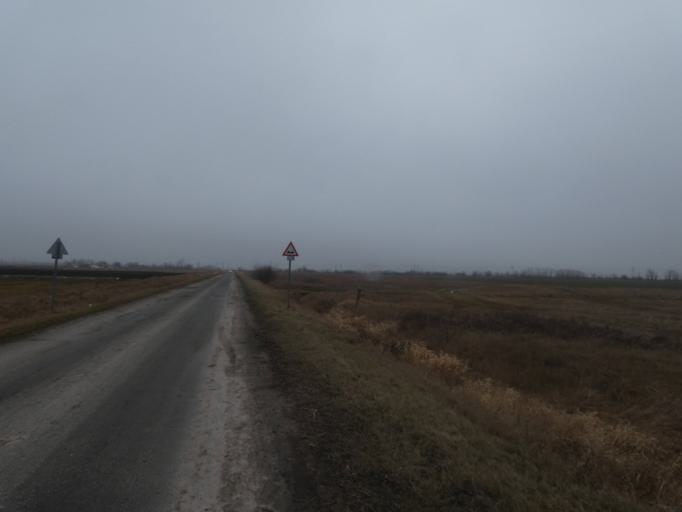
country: HU
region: Pest
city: Tapiogyorgye
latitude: 47.3156
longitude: 19.9707
